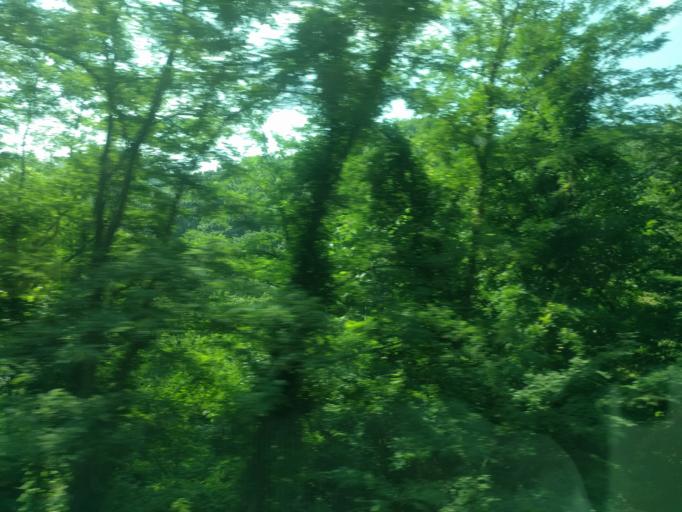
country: JP
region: Fukushima
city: Inawashiro
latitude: 37.4959
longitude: 140.2109
